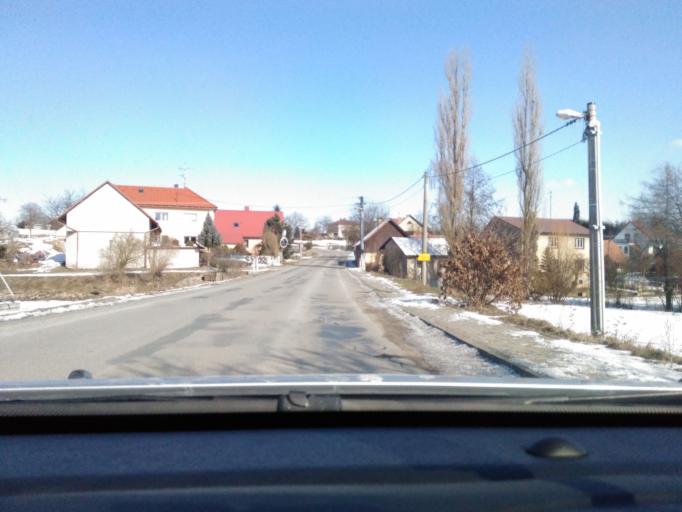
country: CZ
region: Vysocina
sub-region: Okres Zd'ar nad Sazavou
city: Nove Mesto na Morave
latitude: 49.5295
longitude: 16.0397
